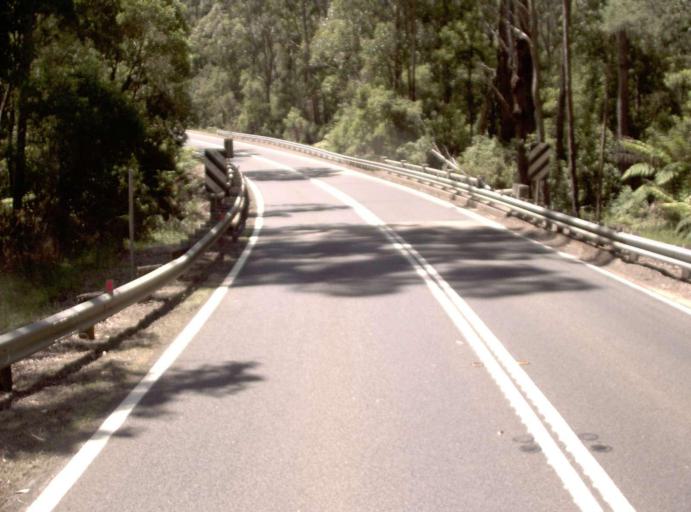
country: AU
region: New South Wales
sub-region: Bombala
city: Bombala
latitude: -37.5912
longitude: 148.9184
